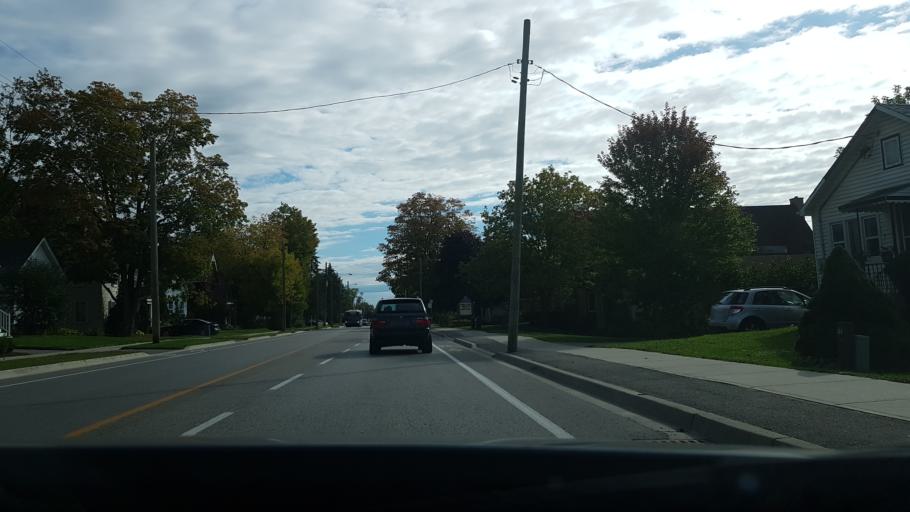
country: CA
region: Ontario
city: Orillia
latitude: 44.6092
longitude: -79.4304
